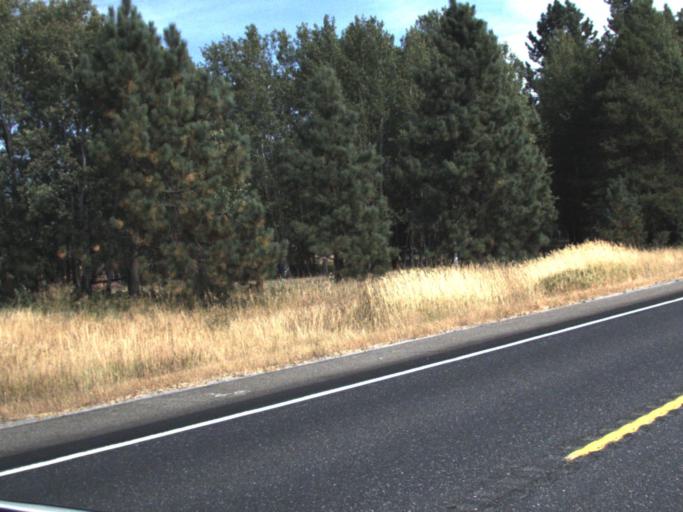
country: US
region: Washington
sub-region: Spokane County
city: Deer Park
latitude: 47.9937
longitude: -117.5579
